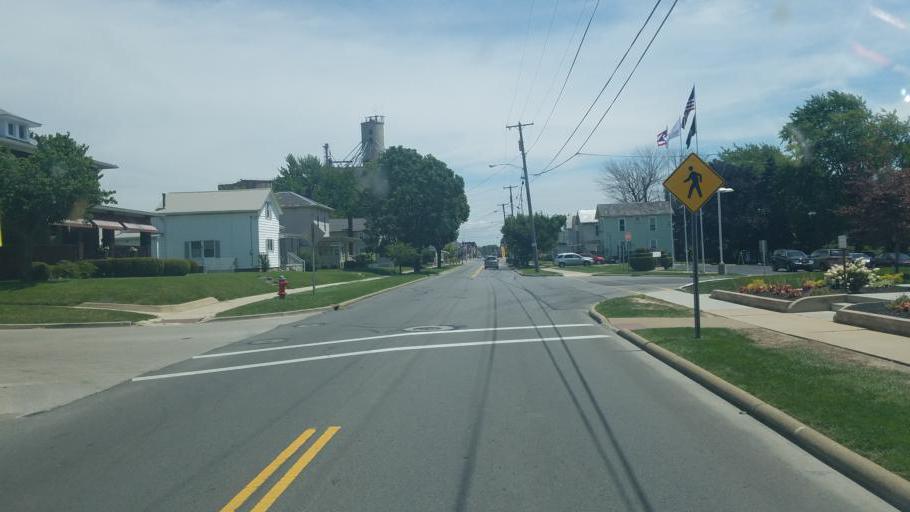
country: US
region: Ohio
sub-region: Richland County
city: Shelby
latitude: 40.8813
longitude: -82.6679
